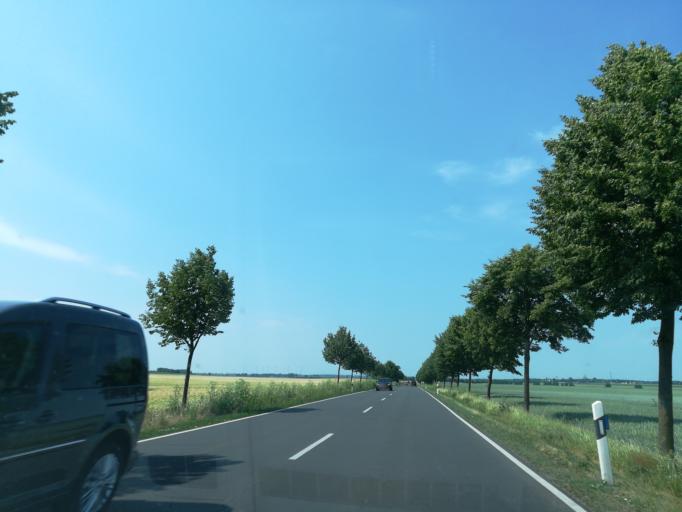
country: DE
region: Saxony-Anhalt
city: Schneidlingen
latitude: 51.9095
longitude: 11.4310
